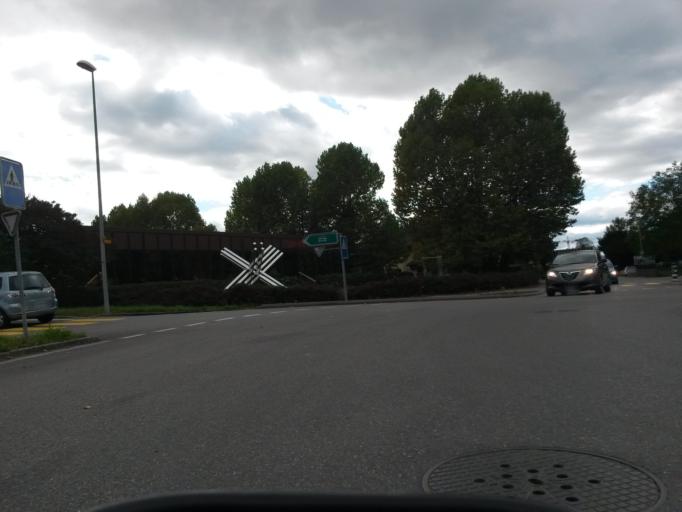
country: CH
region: Bern
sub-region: Seeland District
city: Worben
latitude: 47.1095
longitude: 7.3013
